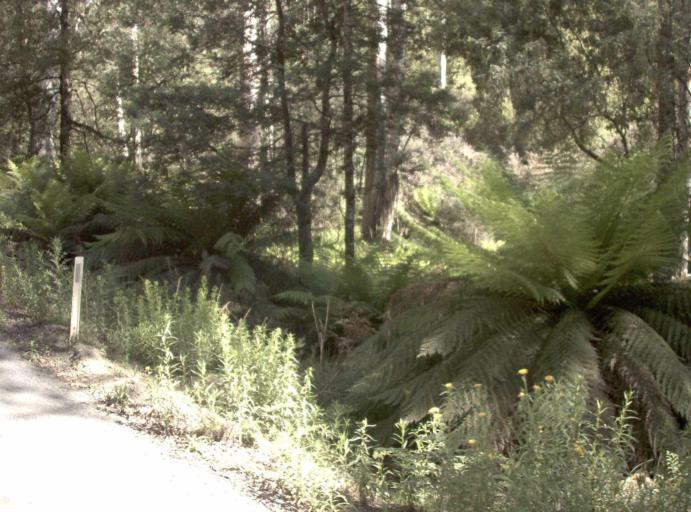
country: AU
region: New South Wales
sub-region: Bombala
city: Bombala
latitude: -37.2081
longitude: 148.7408
